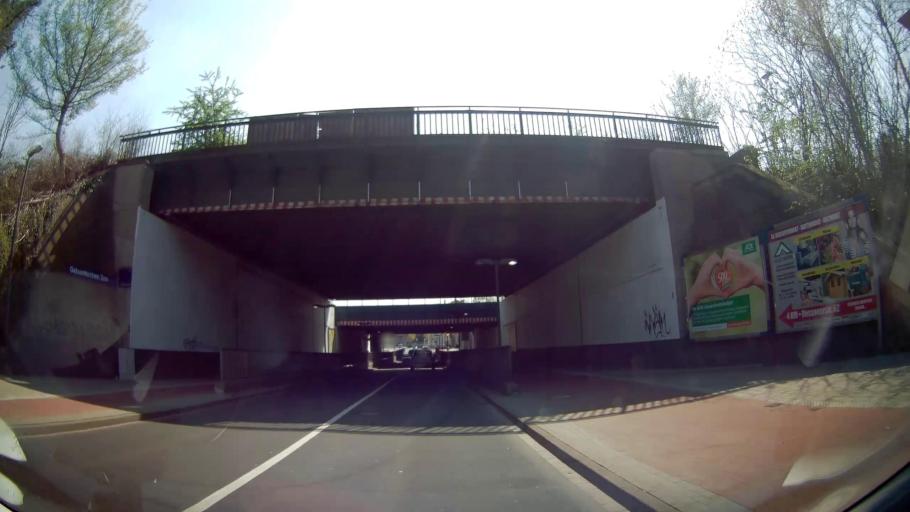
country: DE
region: North Rhine-Westphalia
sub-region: Regierungsbezirk Munster
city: Gelsenkirchen
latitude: 51.5383
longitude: 7.1098
